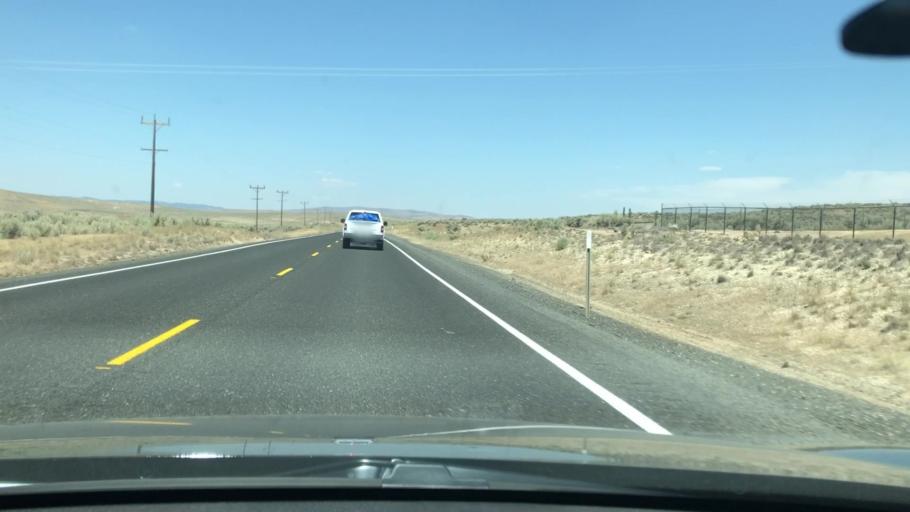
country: US
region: Idaho
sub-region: Owyhee County
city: Murphy
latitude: 43.0021
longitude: -117.0640
